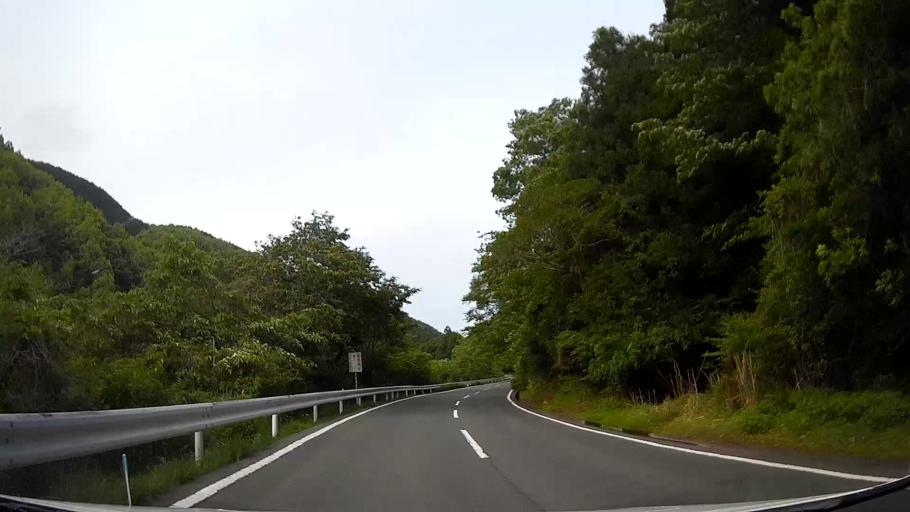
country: JP
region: Shizuoka
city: Ito
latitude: 34.9758
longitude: 139.0502
